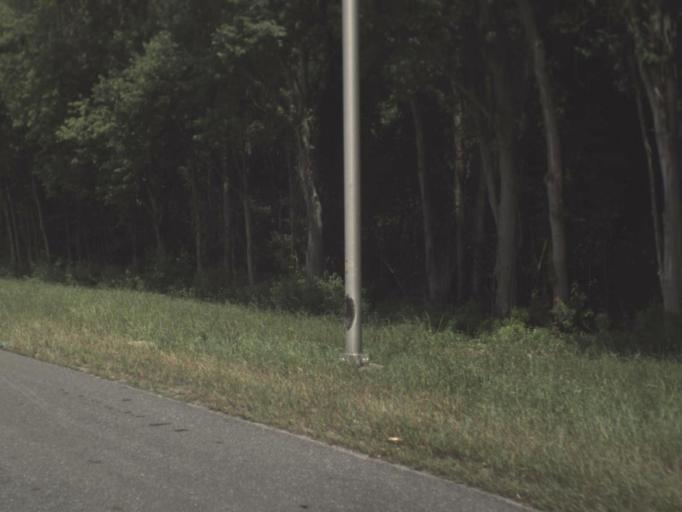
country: US
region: Florida
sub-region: Clay County
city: Bellair-Meadowbrook Terrace
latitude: 30.2267
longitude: -81.7626
